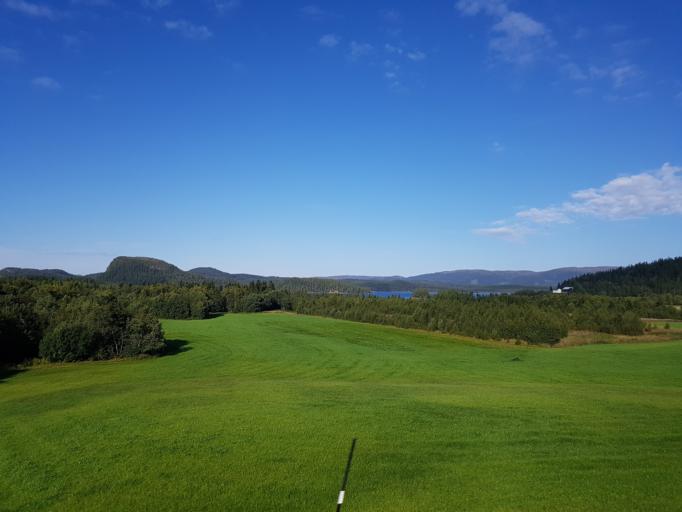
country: NO
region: Sor-Trondelag
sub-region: Trondheim
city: Trondheim
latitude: 63.6013
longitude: 10.2241
